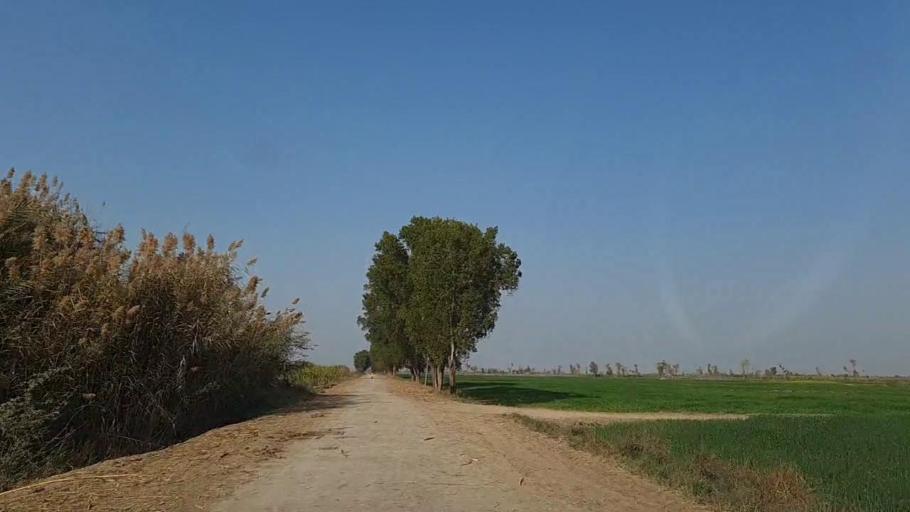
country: PK
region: Sindh
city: Daur
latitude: 26.4802
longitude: 68.2972
